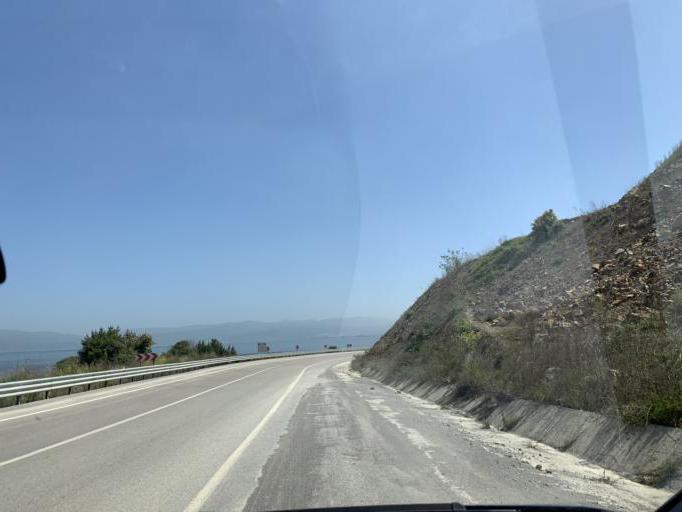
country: TR
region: Bursa
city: Niluefer
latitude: 40.3574
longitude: 28.9918
